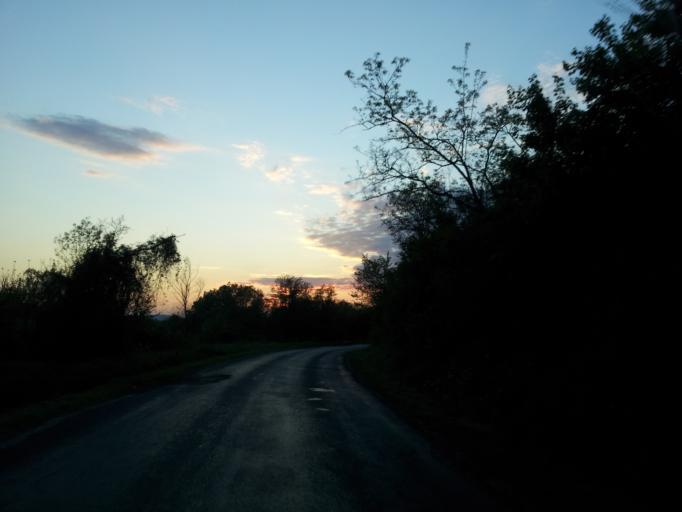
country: HU
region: Pest
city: Perbal
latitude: 47.6396
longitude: 18.7489
